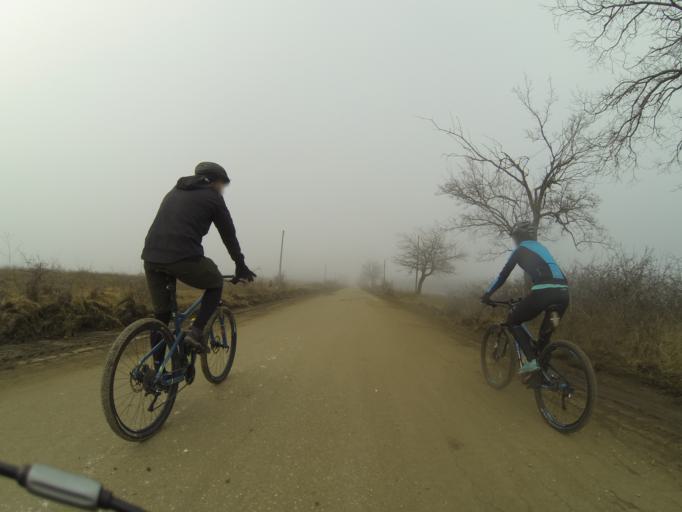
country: RO
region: Mehedinti
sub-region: Comuna Baclesu
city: Baclesu
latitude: 44.4850
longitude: 23.1018
